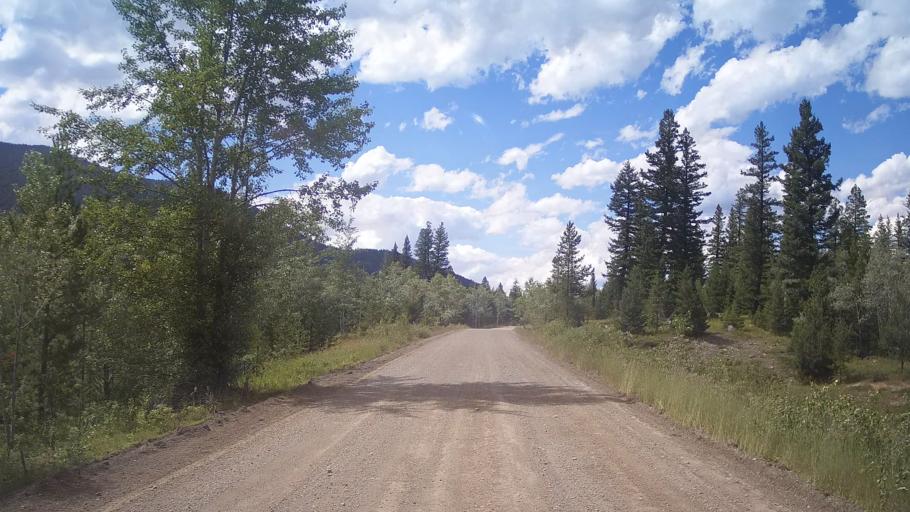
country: CA
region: British Columbia
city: Lillooet
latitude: 51.3254
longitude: -121.8768
